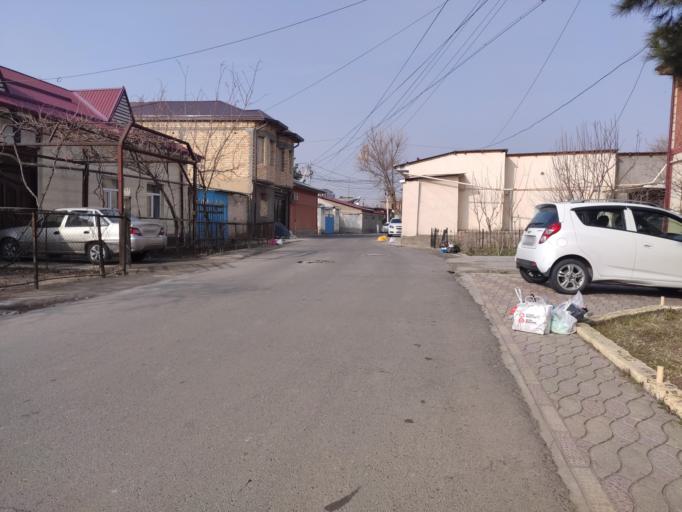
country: UZ
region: Toshkent Shahri
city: Tashkent
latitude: 41.2728
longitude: 69.2718
